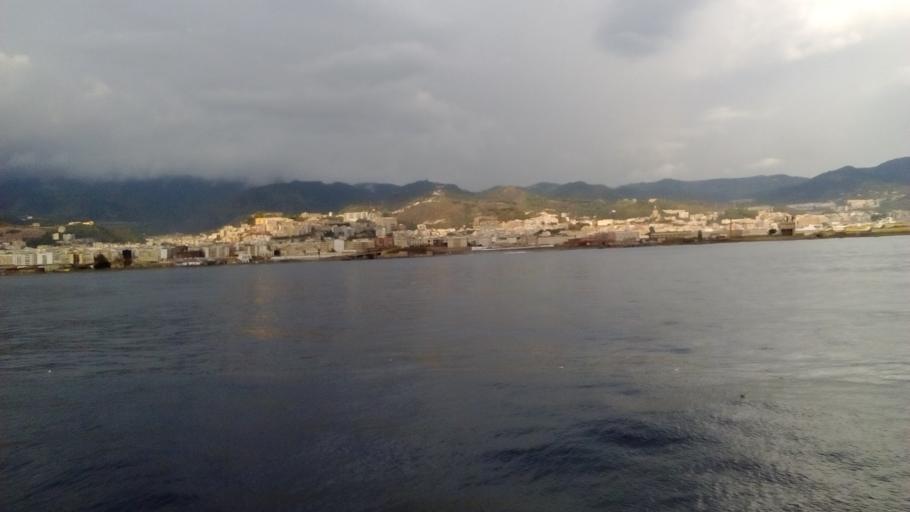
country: IT
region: Sicily
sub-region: Messina
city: Messina
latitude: 38.1773
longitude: 15.5743
